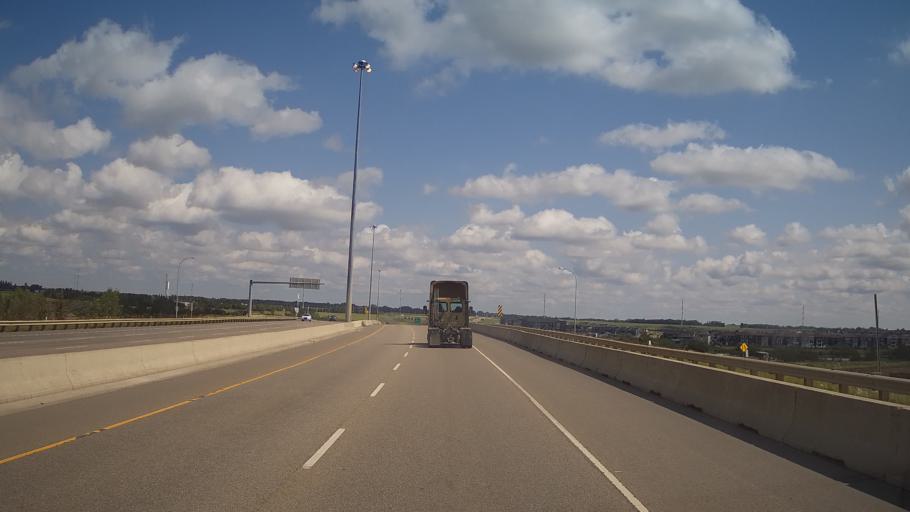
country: CA
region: Alberta
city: Sherwood Park
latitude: 53.4821
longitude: -113.3666
